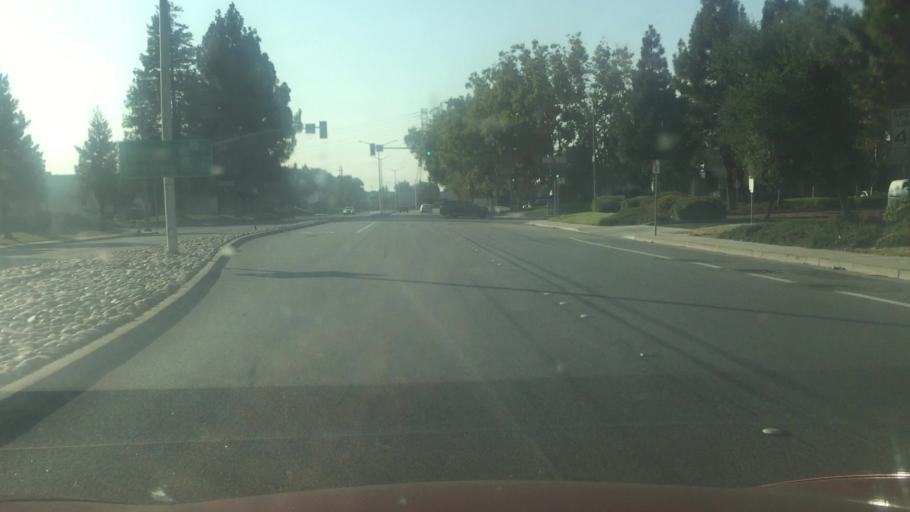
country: US
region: California
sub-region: Alameda County
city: Fremont
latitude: 37.5047
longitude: -121.9582
